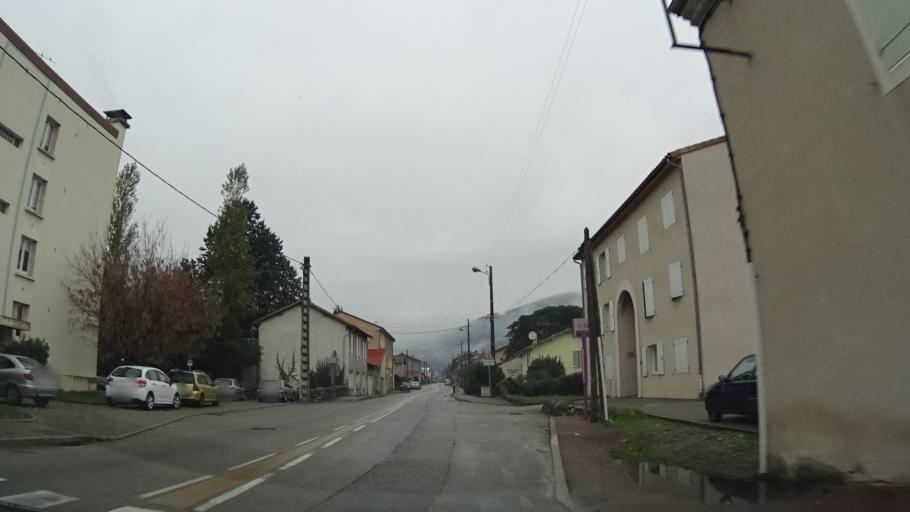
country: FR
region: Rhone-Alpes
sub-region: Departement de l'Ardeche
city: Labegude
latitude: 44.6514
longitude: 4.3214
